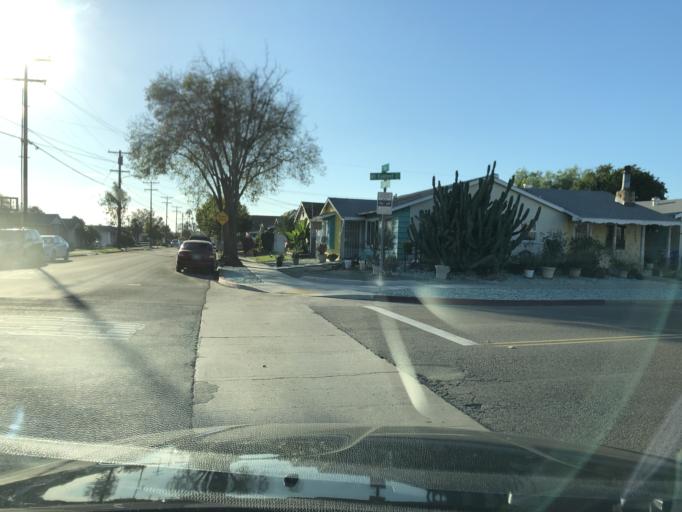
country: US
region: California
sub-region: San Diego County
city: La Jolla
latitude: 32.8186
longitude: -117.1856
